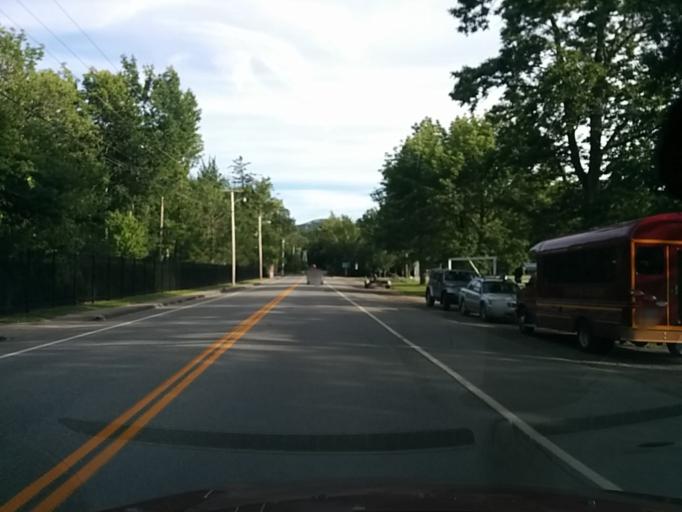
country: US
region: Maine
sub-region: Hancock County
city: Bar Harbor
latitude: 44.3827
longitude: -68.2030
